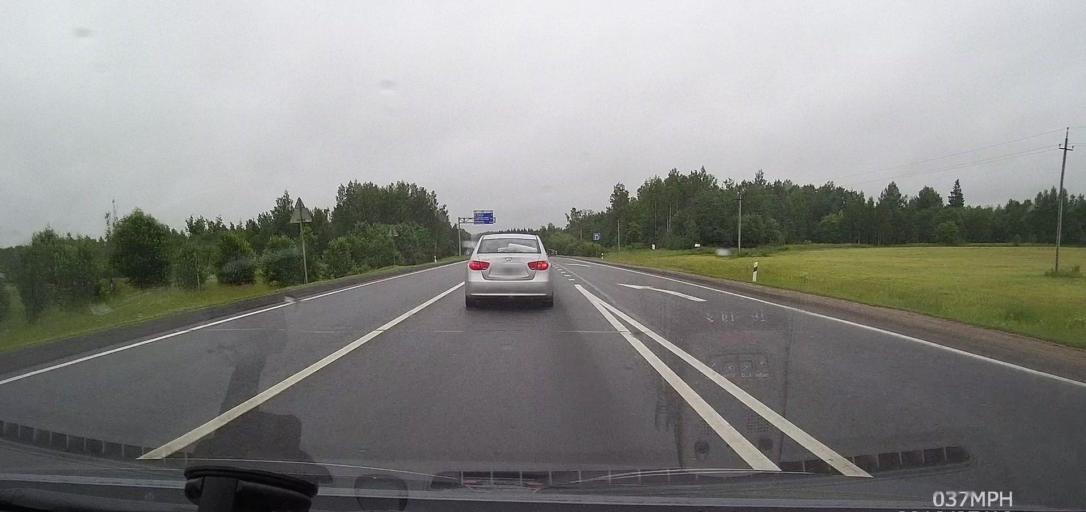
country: RU
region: Leningrad
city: Staraya Ladoga
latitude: 60.0119
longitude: 32.1556
